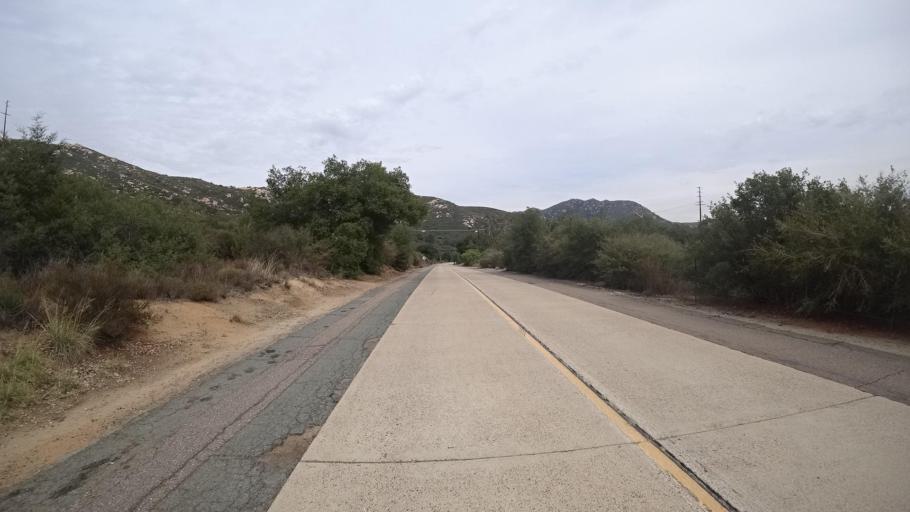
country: US
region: California
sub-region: San Diego County
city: Descanso
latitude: 32.8413
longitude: -116.6310
